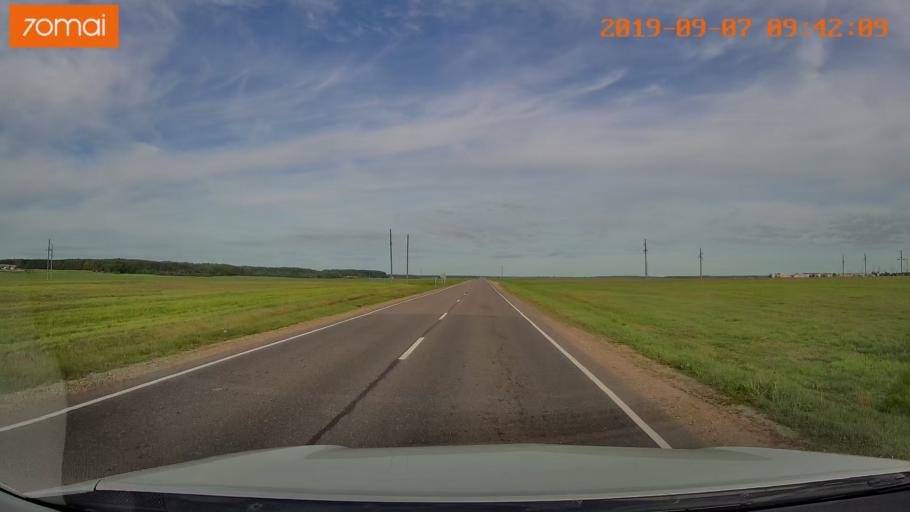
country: BY
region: Grodnenskaya
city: Iwye
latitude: 53.9164
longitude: 25.7653
